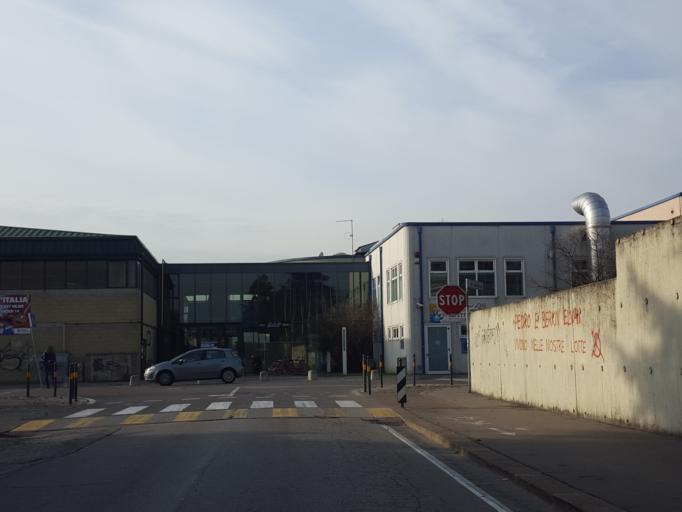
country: IT
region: Veneto
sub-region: Provincia di Vicenza
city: Vicenza
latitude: 45.5601
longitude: 11.5322
